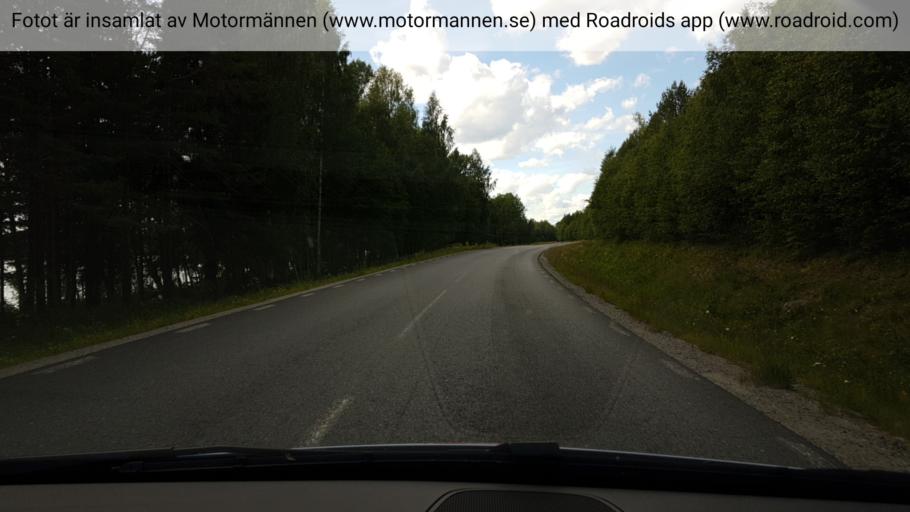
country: SE
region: Jaemtland
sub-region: Braecke Kommun
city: Braecke
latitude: 62.4011
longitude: 15.0251
